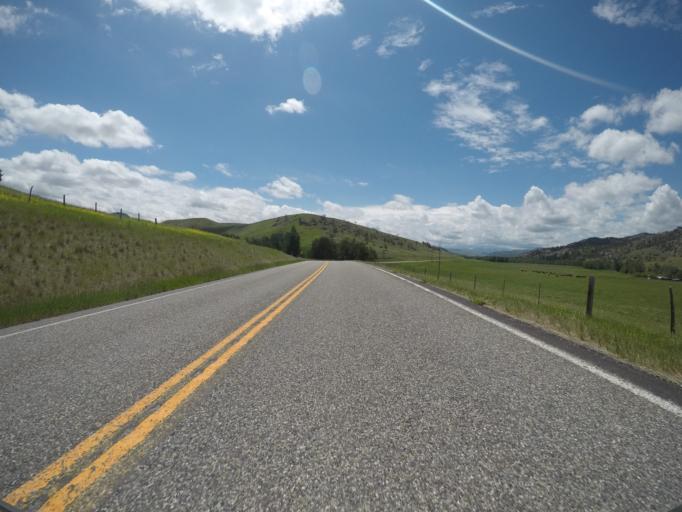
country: US
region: Montana
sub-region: Sweet Grass County
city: Big Timber
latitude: 45.7109
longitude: -110.0050
